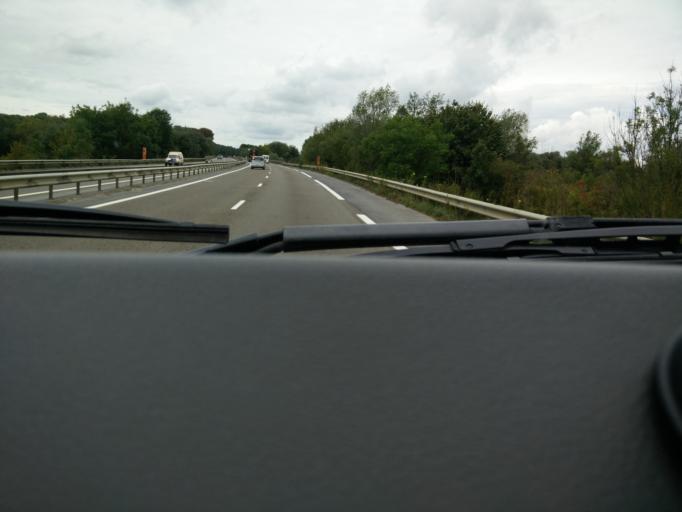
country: FR
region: Champagne-Ardenne
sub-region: Departement des Ardennes
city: Sedan
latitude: 49.6876
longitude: 4.9471
